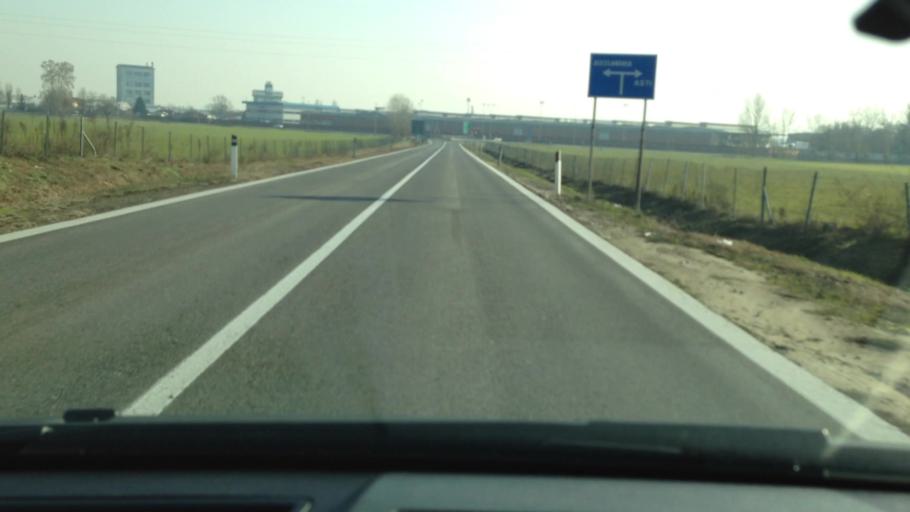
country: IT
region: Piedmont
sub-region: Provincia di Alessandria
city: Quattordio
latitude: 44.9015
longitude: 8.4182
